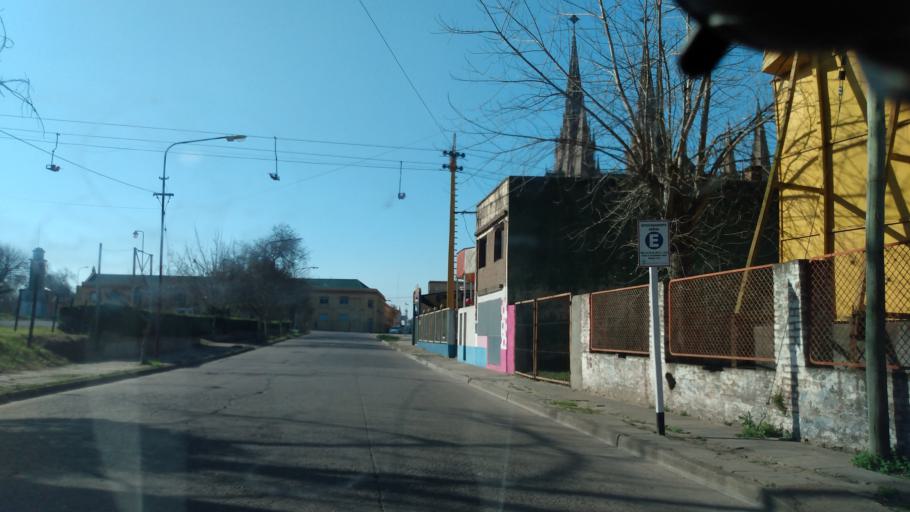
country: AR
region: Buenos Aires
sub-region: Partido de Lujan
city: Lujan
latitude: -34.5659
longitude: -59.1225
